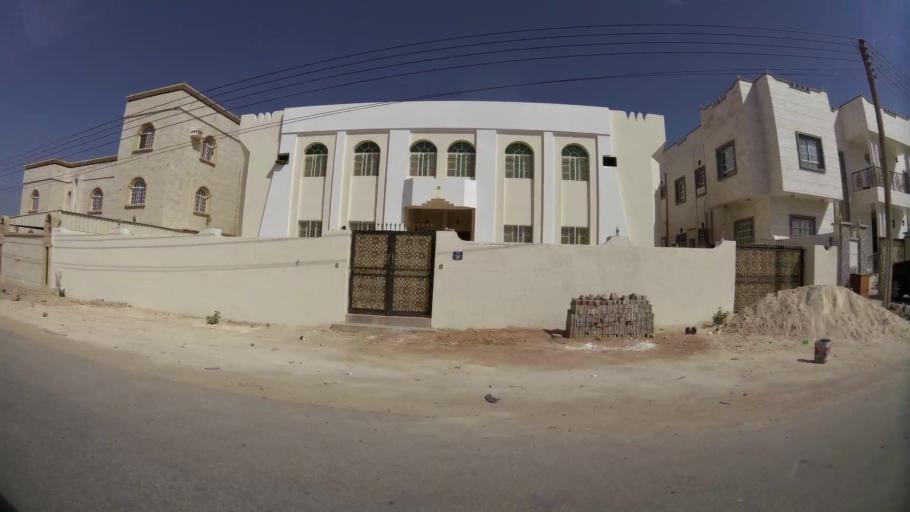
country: OM
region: Zufar
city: Salalah
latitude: 17.0038
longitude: 54.0189
